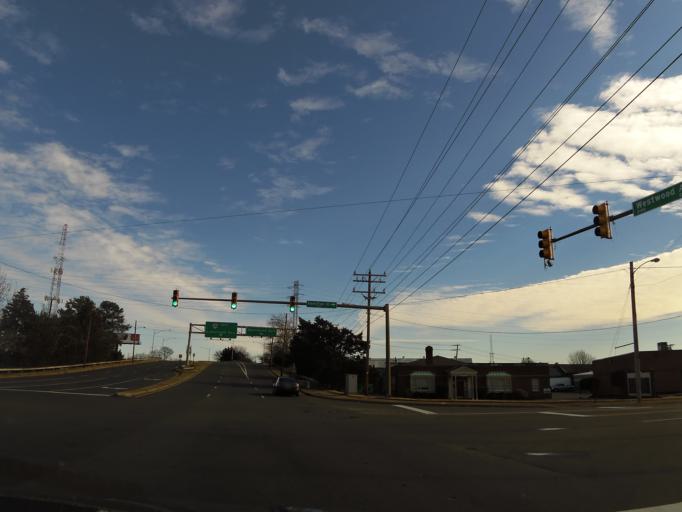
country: US
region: Virginia
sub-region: City of Richmond
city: Richmond
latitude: 37.5773
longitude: -77.4751
